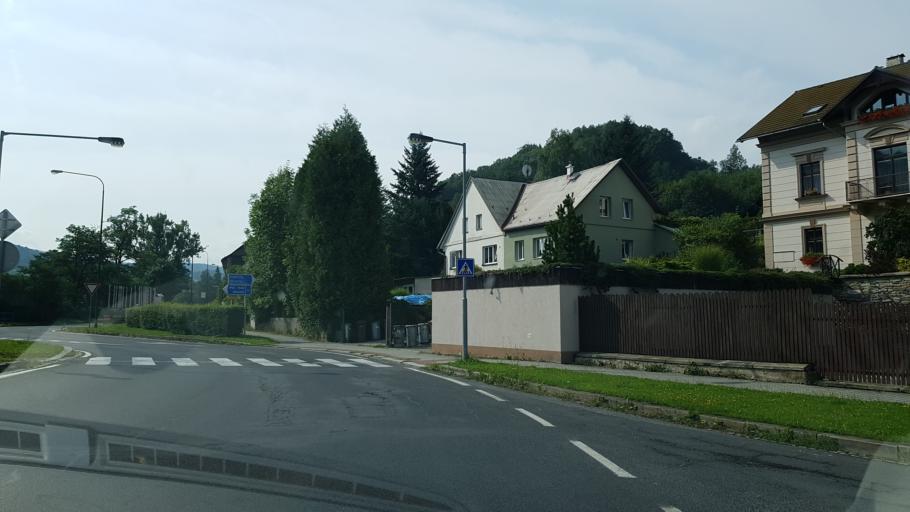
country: CZ
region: Olomoucky
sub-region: Okres Jesenik
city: Jesenik
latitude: 50.2241
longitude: 17.2074
